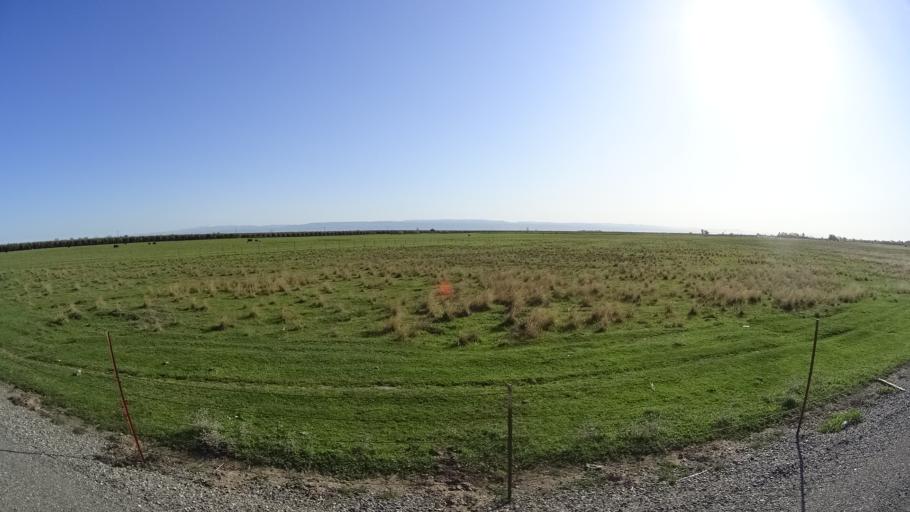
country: US
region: California
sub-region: Glenn County
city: Hamilton City
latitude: 39.7487
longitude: -122.0994
